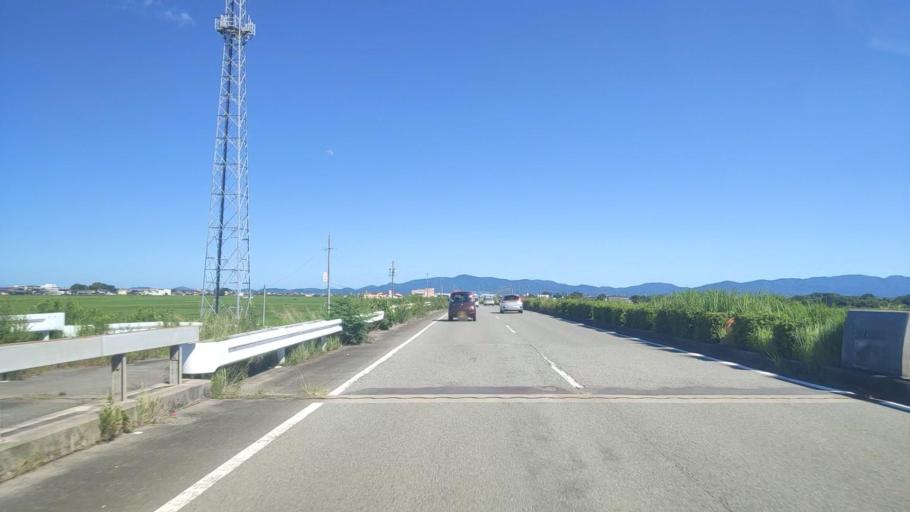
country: JP
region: Mie
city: Ise
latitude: 34.5631
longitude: 136.6412
